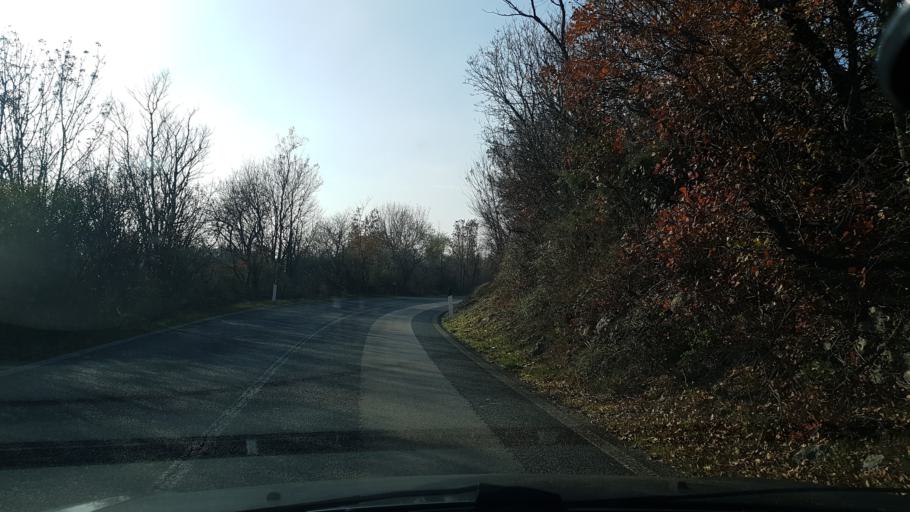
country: IT
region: Friuli Venezia Giulia
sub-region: Provincia di Gorizia
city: Doberdo del Lago
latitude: 45.8387
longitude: 13.5279
